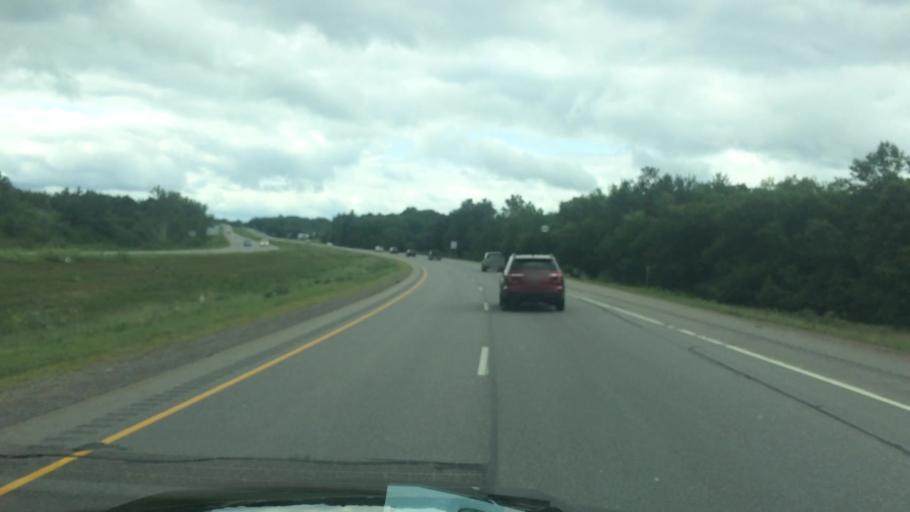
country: US
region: Wisconsin
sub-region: Marathon County
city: Mosinee
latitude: 44.8052
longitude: -89.6774
